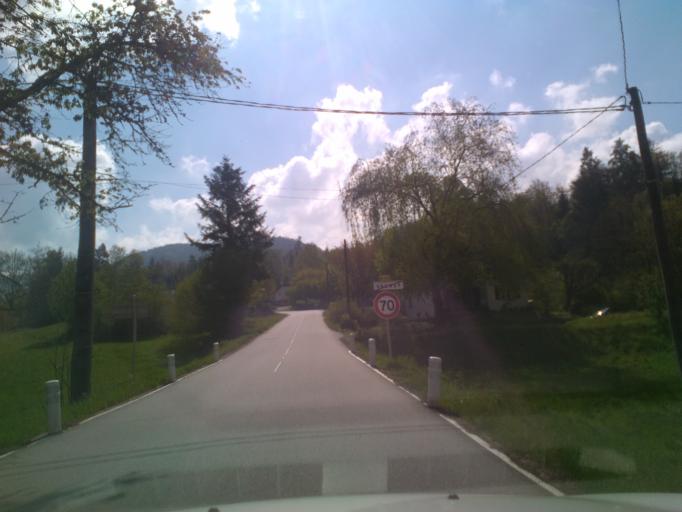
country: FR
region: Lorraine
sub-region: Departement des Vosges
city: Vagney
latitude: 47.9981
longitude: 6.7269
